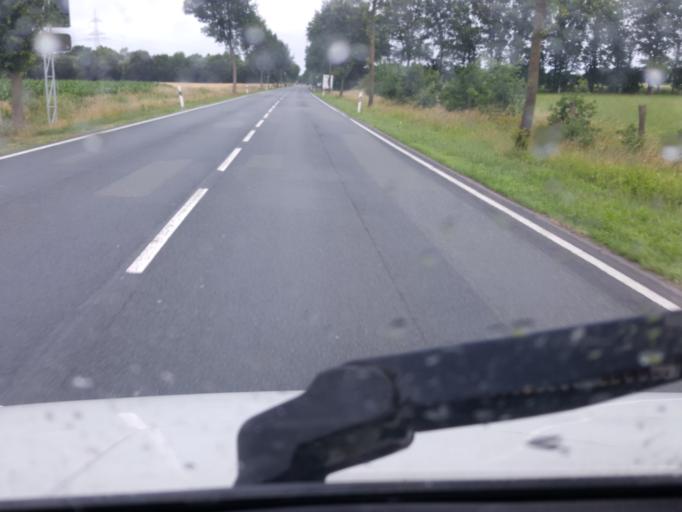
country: DE
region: Lower Saxony
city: Raddestorf
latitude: 52.4174
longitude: 8.9492
